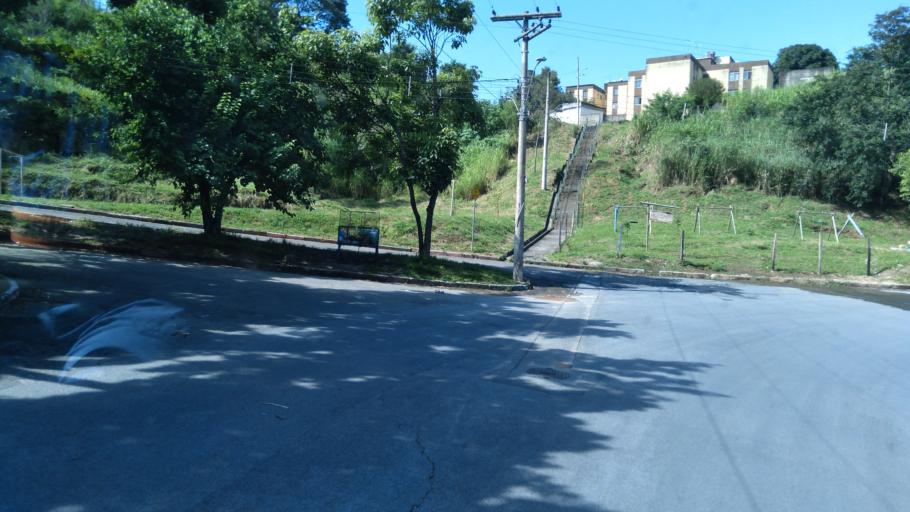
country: BR
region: Minas Gerais
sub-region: Santa Luzia
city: Santa Luzia
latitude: -19.8252
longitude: -43.9015
